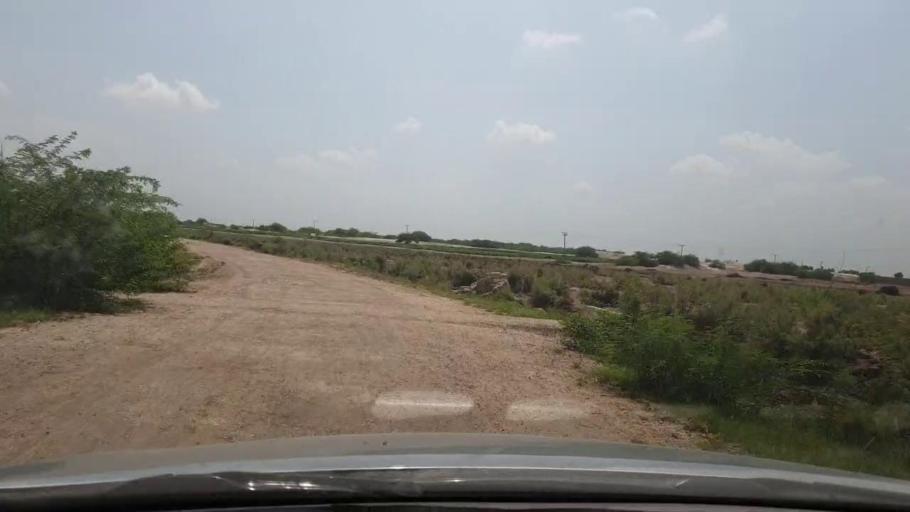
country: PK
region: Sindh
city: Kot Diji
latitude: 27.3884
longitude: 68.7156
